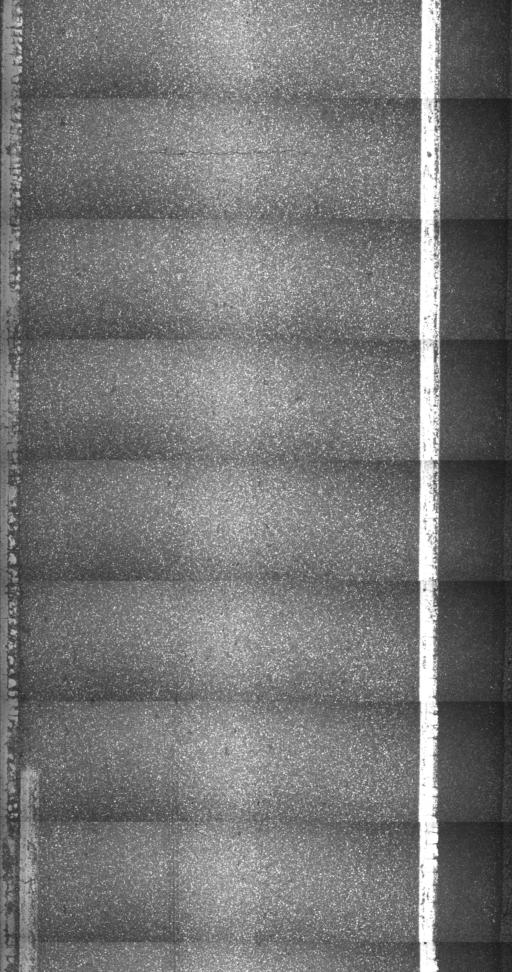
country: US
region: Vermont
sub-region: Orange County
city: Chelsea
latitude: 43.8182
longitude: -72.5113
